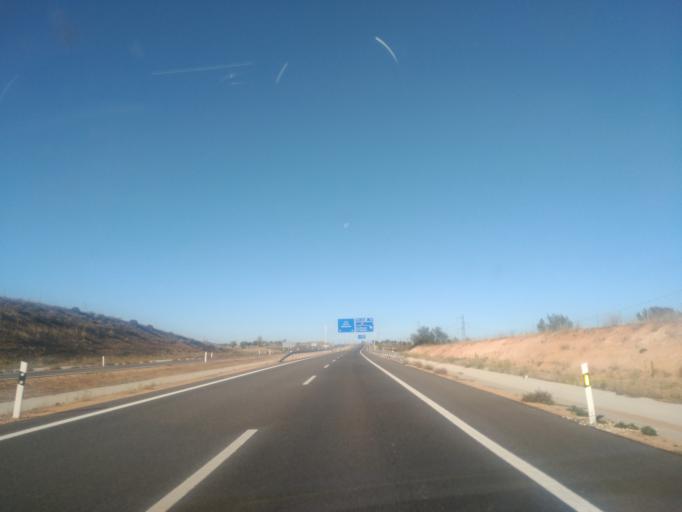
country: ES
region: Castille and Leon
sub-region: Provincia de Burgos
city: Fuentespina
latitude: 41.6403
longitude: -3.6753
